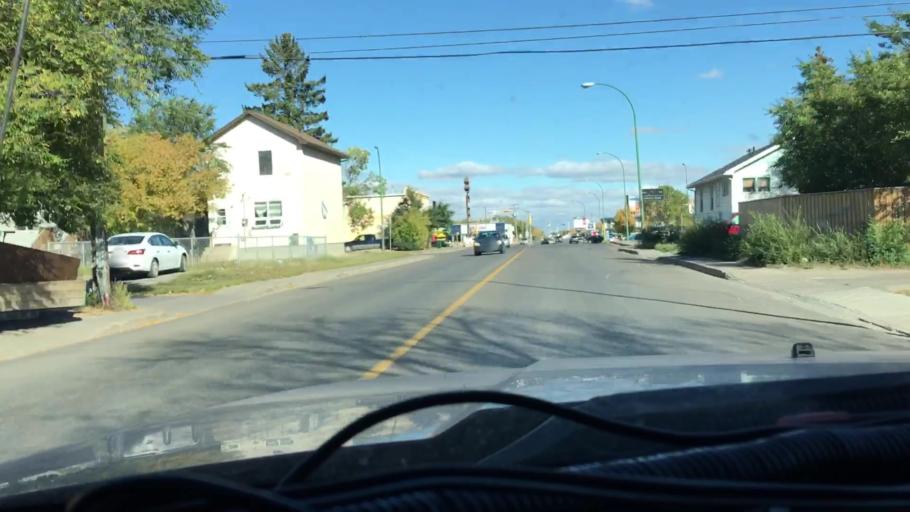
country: CA
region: Saskatchewan
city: Regina
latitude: 50.4629
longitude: -104.6206
